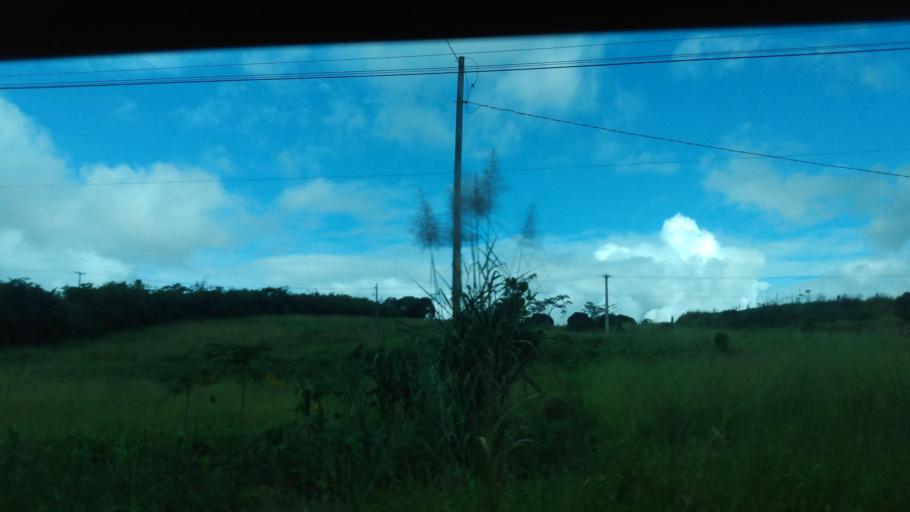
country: BR
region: Pernambuco
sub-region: Quipapa
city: Quipapa
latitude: -8.7876
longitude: -35.9624
